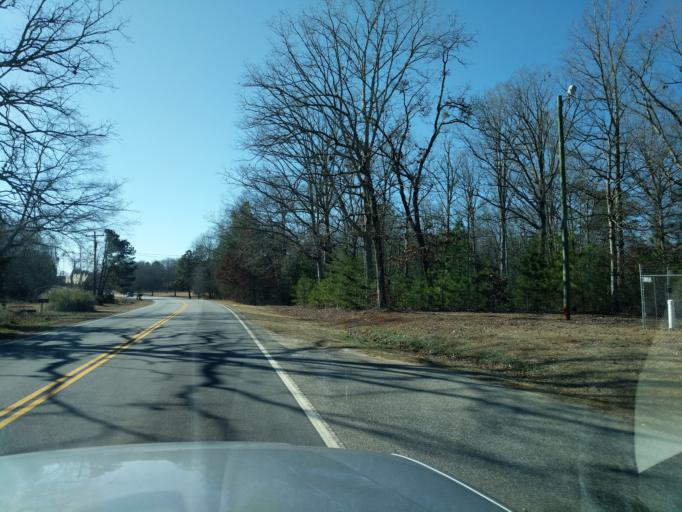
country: US
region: South Carolina
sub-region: Anderson County
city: Homeland Park
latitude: 34.4456
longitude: -82.7123
